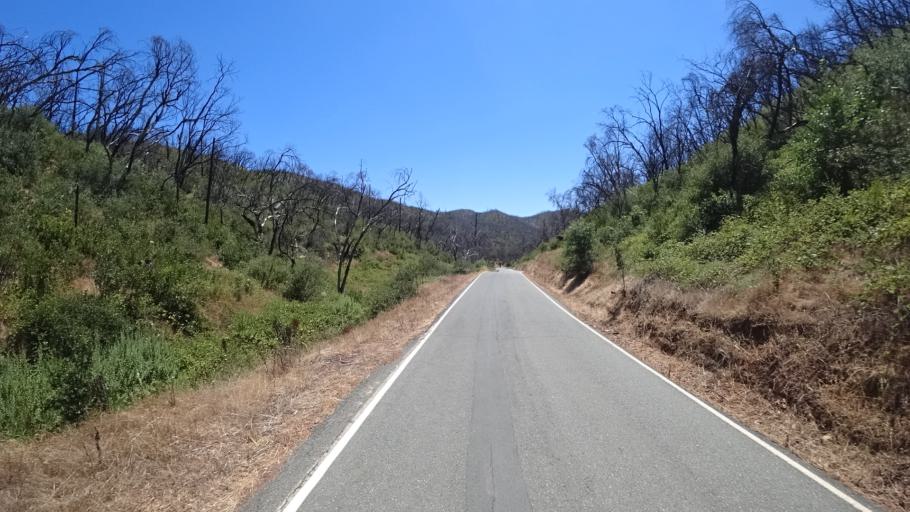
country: US
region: California
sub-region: Calaveras County
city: San Andreas
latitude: 38.2881
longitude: -120.6707
